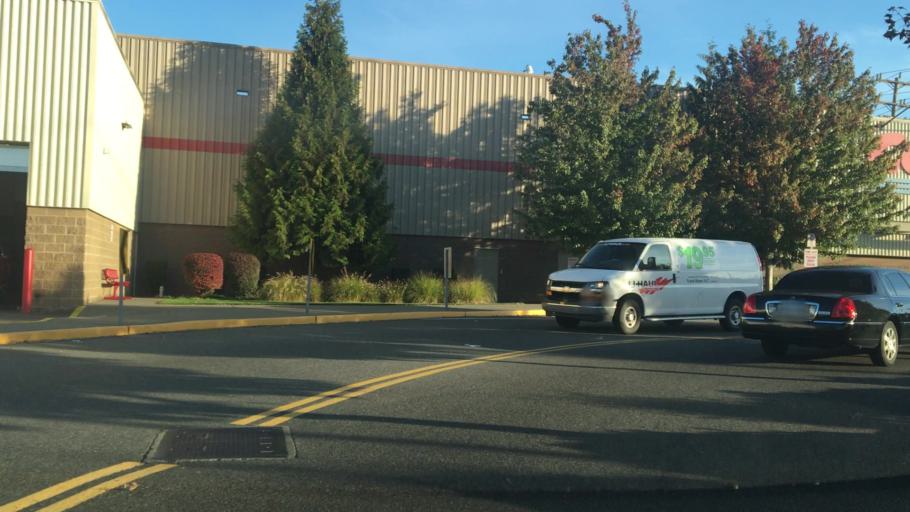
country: US
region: Washington
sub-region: King County
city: Seattle
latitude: 47.5645
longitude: -122.3302
